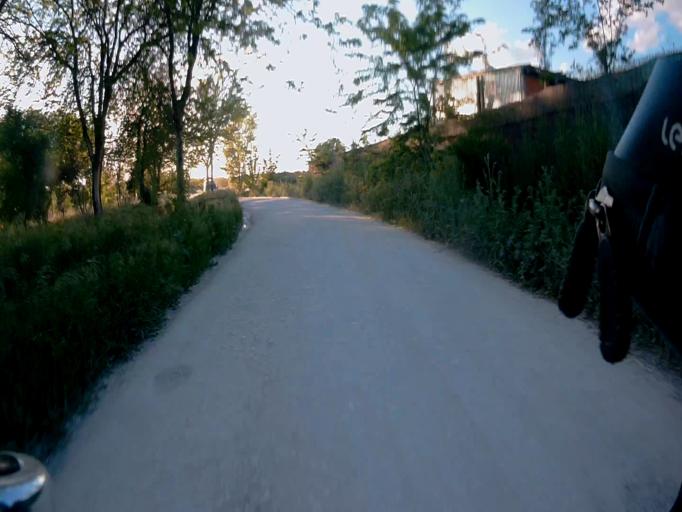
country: ES
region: Madrid
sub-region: Provincia de Madrid
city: Leganes
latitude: 40.3273
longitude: -3.7945
